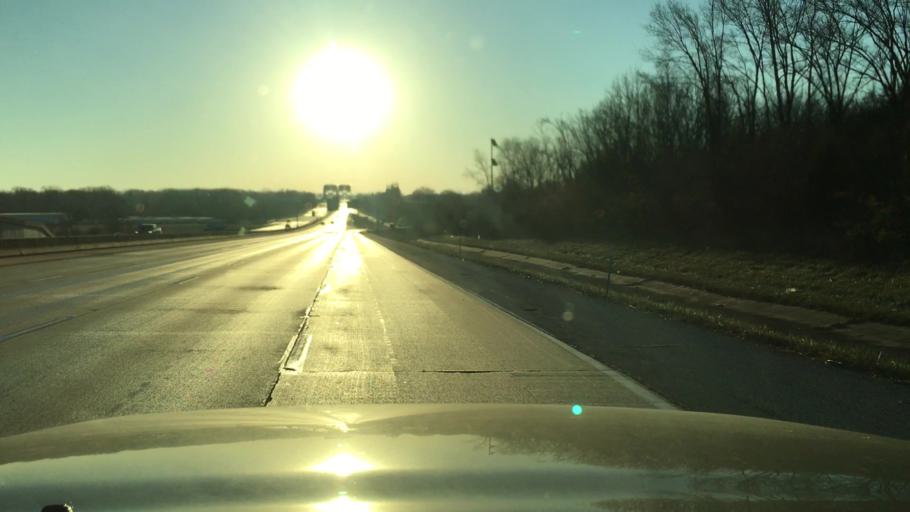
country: US
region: Missouri
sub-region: Saint Charles County
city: Saint Charles
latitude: 38.8061
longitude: -90.4805
